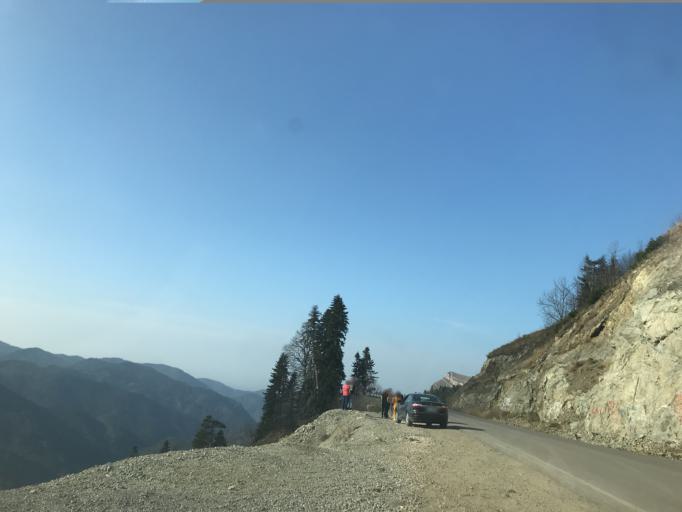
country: TR
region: Bolu
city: Bolu
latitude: 40.8836
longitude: 31.6832
